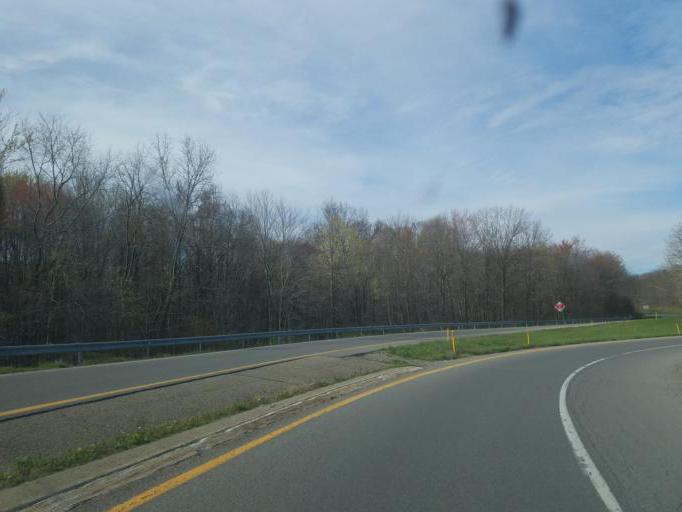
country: US
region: Pennsylvania
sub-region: Mercer County
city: Mercer
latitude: 41.2664
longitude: -80.1684
